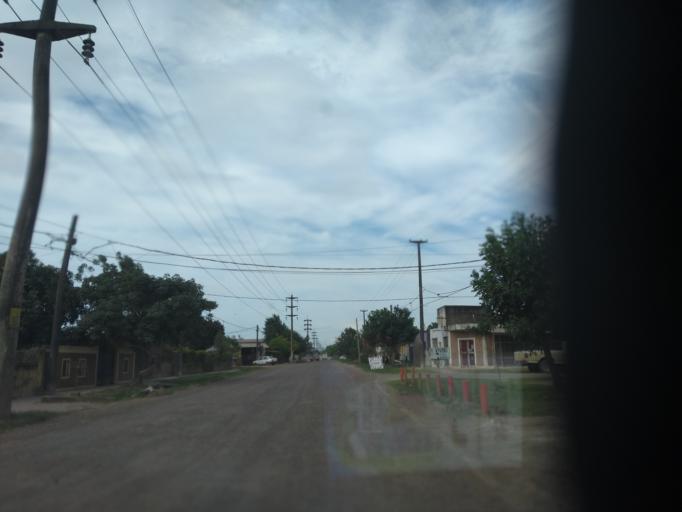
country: AR
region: Chaco
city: Resistencia
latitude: -27.4756
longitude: -58.9709
